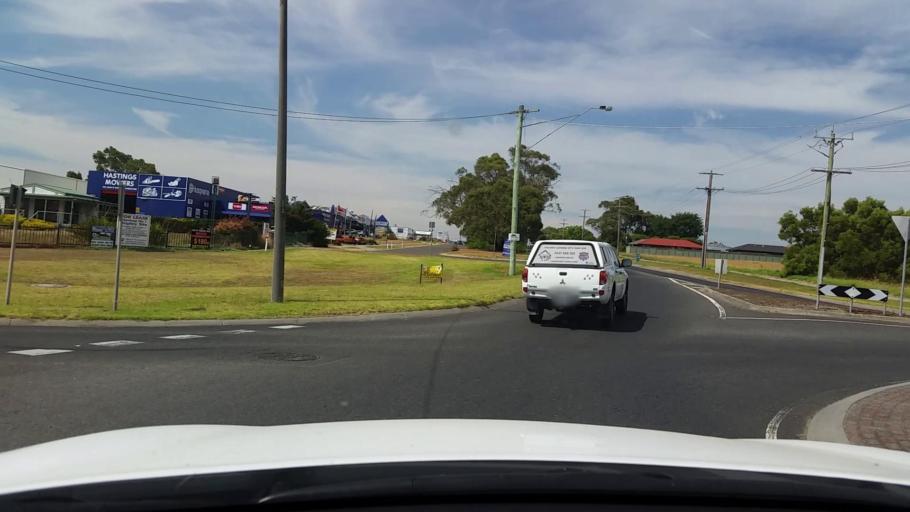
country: AU
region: Victoria
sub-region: Mornington Peninsula
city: Hastings
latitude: -38.2999
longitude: 145.1838
